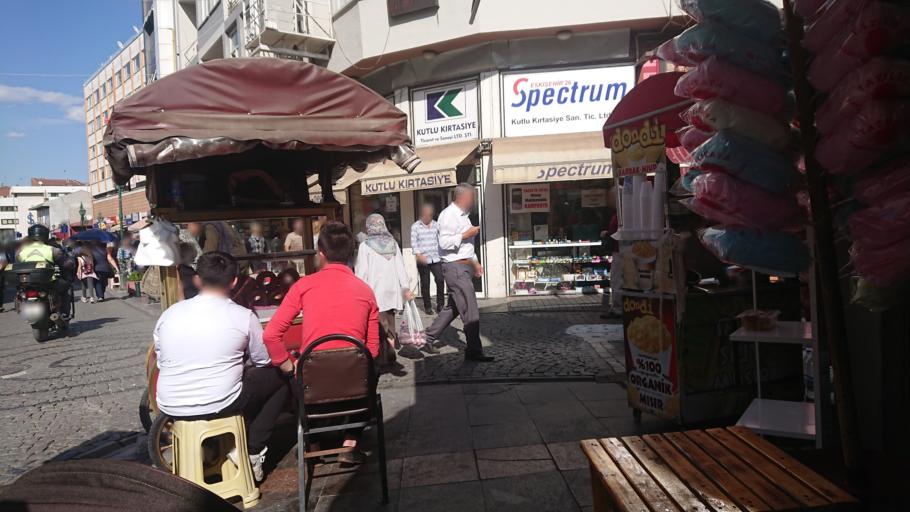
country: TR
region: Eskisehir
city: Eskisehir
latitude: 39.7743
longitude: 30.5190
